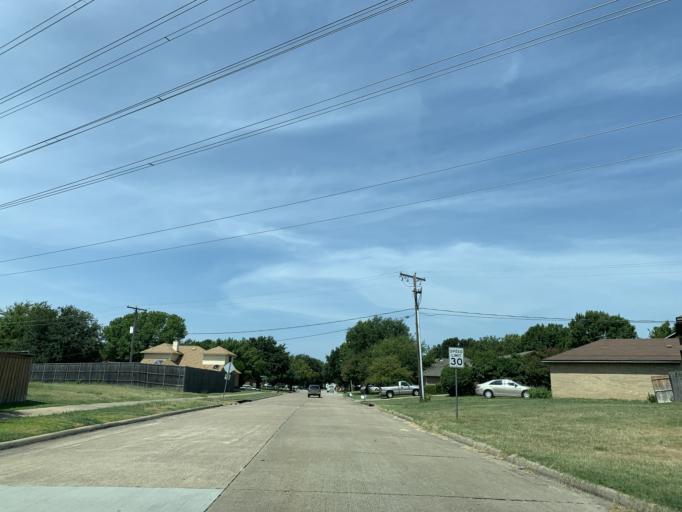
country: US
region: Texas
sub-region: Dallas County
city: Grand Prairie
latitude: 32.6664
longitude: -97.0364
